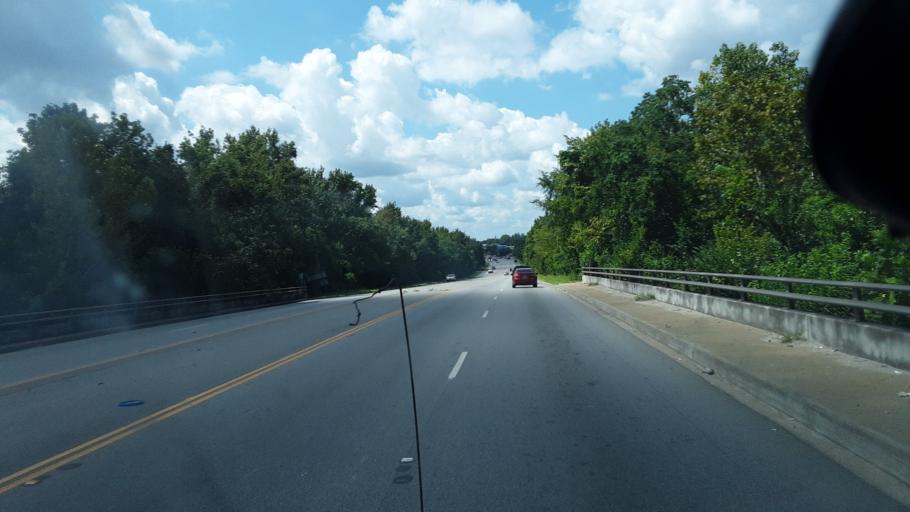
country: US
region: South Carolina
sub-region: Berkeley County
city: Moncks Corner
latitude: 33.2146
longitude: -79.9758
